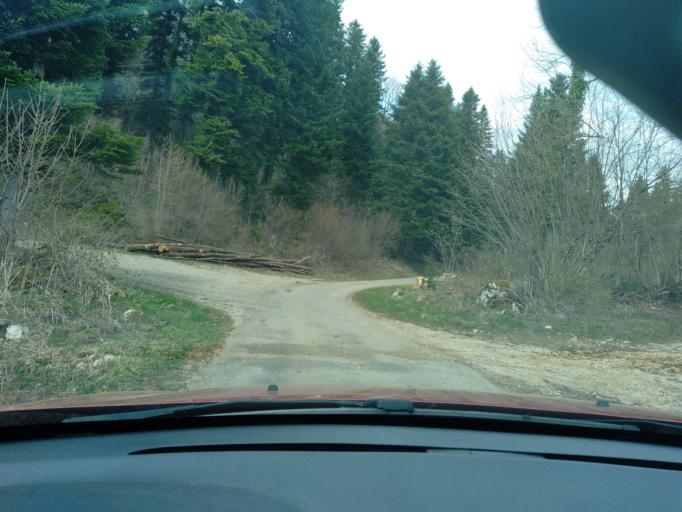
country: FR
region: Franche-Comte
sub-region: Departement du Jura
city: Moirans-en-Montagne
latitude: 46.4657
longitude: 5.7490
